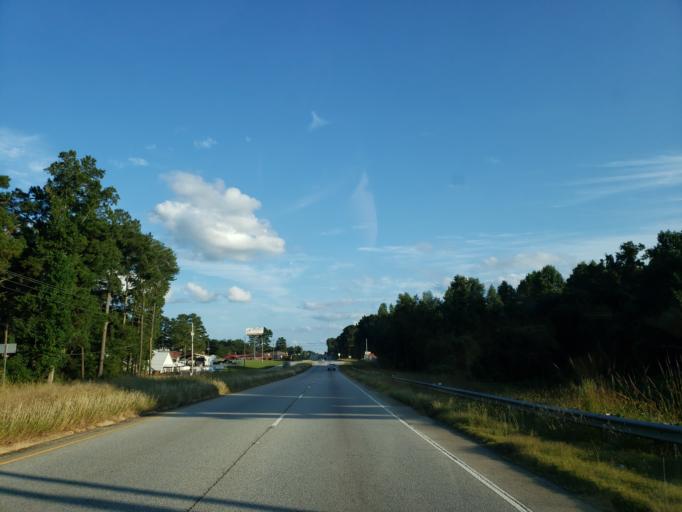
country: US
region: Georgia
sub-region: Carroll County
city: Mount Zion
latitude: 33.6541
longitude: -85.1403
